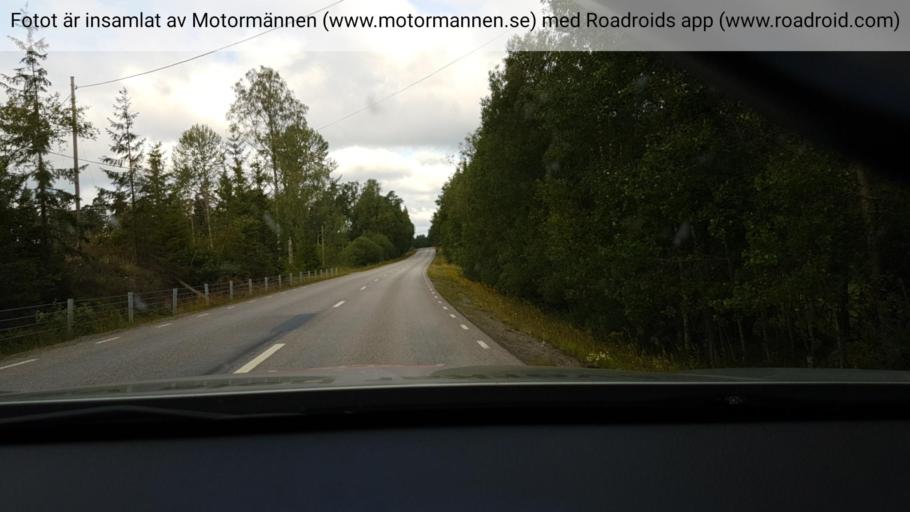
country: SE
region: Stockholm
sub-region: Norrtalje Kommun
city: Nykvarn
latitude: 59.9075
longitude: 18.3046
